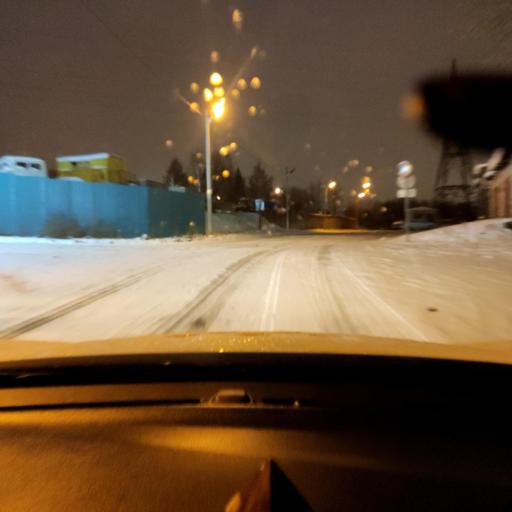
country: RU
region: Tatarstan
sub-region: Gorod Kazan'
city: Kazan
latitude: 55.8130
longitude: 49.0506
